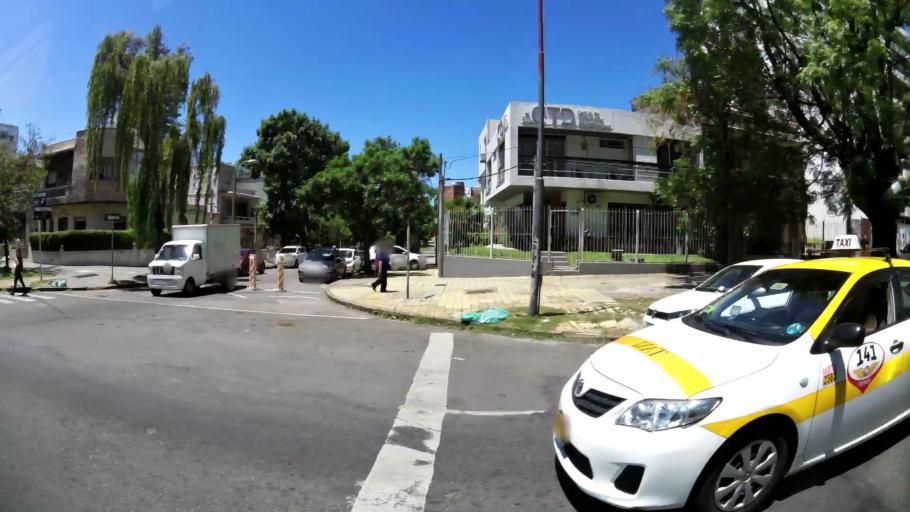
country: UY
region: Montevideo
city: Montevideo
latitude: -34.9006
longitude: -56.1597
